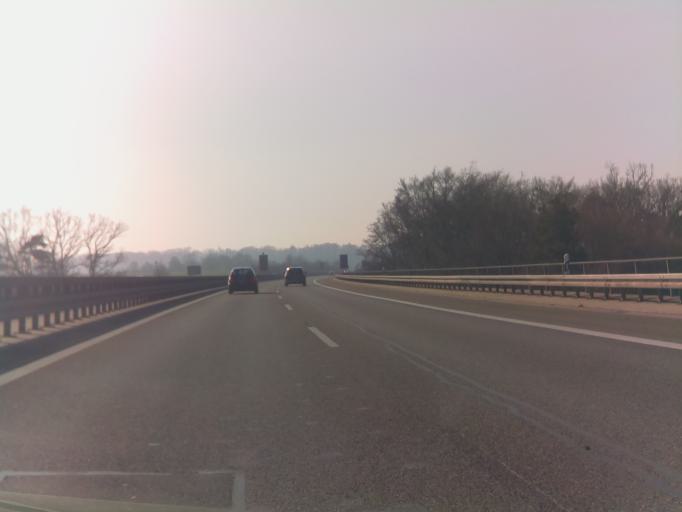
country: DE
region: Baden-Wuerttemberg
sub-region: Regierungsbezirk Stuttgart
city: Bondorf
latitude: 48.5388
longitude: 8.8909
